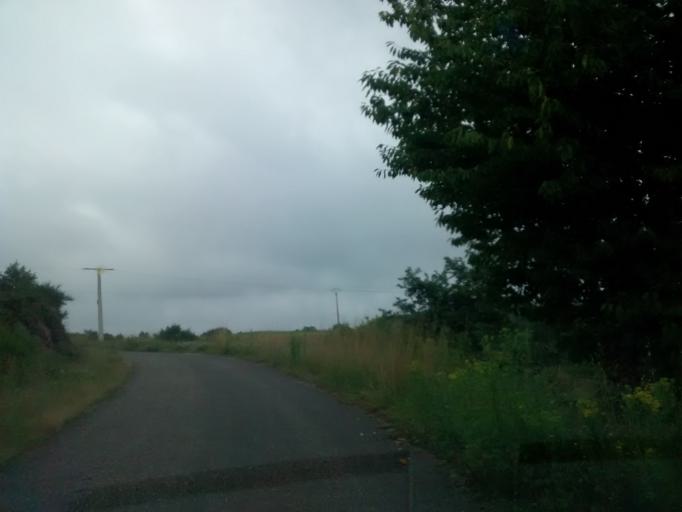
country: ES
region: Galicia
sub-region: Provincia de Ourense
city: Castro Caldelas
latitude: 42.4068
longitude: -7.3989
